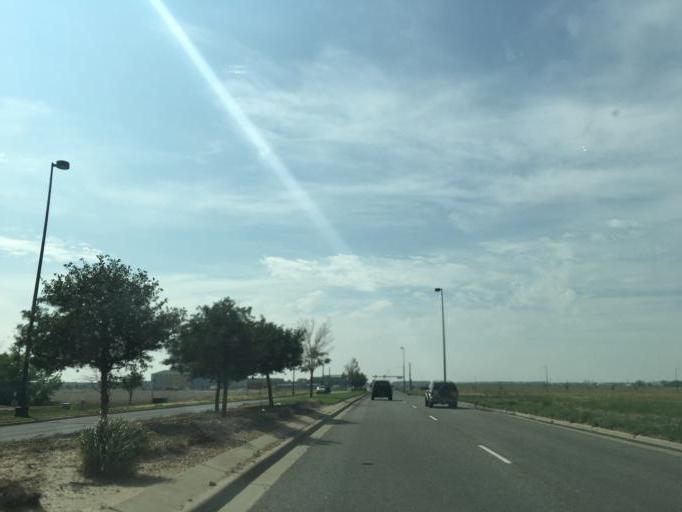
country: US
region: Colorado
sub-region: Adams County
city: Aurora
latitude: 39.8098
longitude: -104.7722
